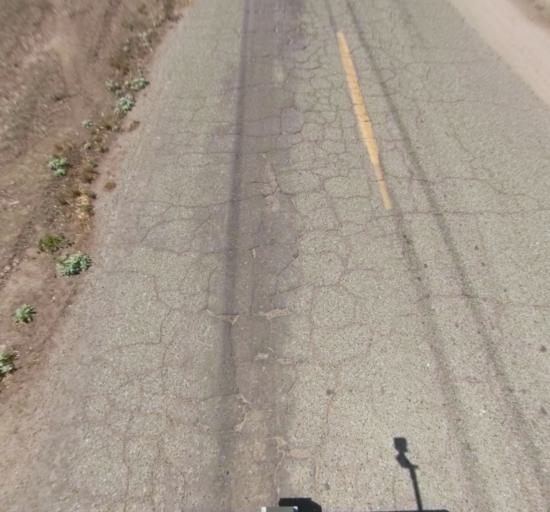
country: US
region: California
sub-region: Madera County
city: Chowchilla
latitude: 37.0796
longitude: -120.3288
